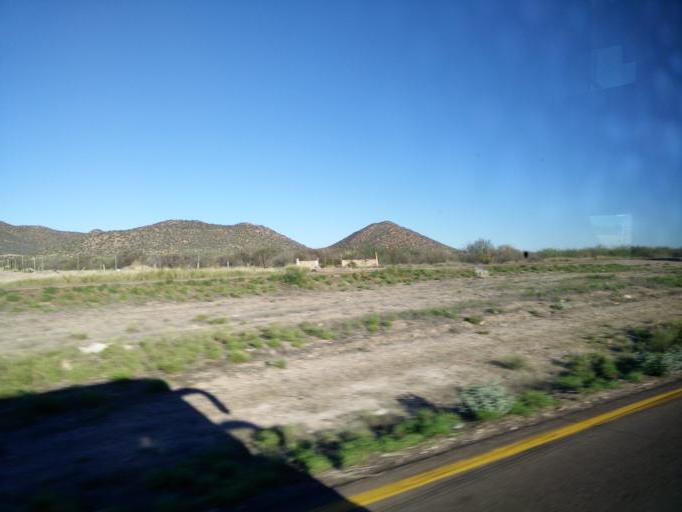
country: MX
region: Sonora
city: Heroica Guaymas
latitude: 28.0036
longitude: -110.9361
